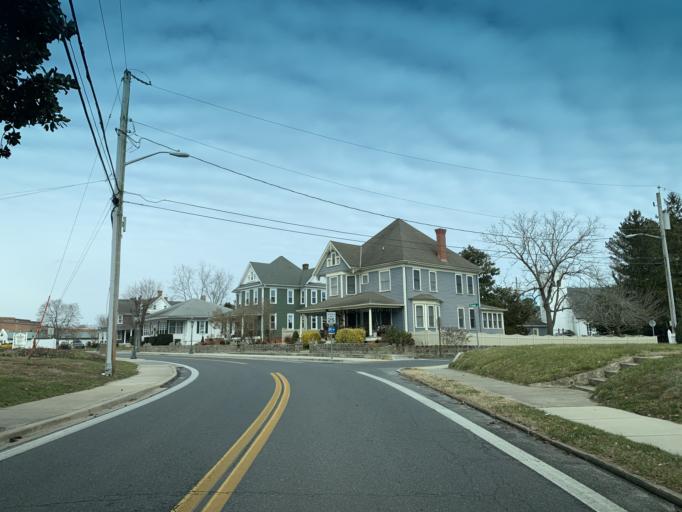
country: US
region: Maryland
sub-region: Worcester County
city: Berlin
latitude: 38.3224
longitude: -75.2182
